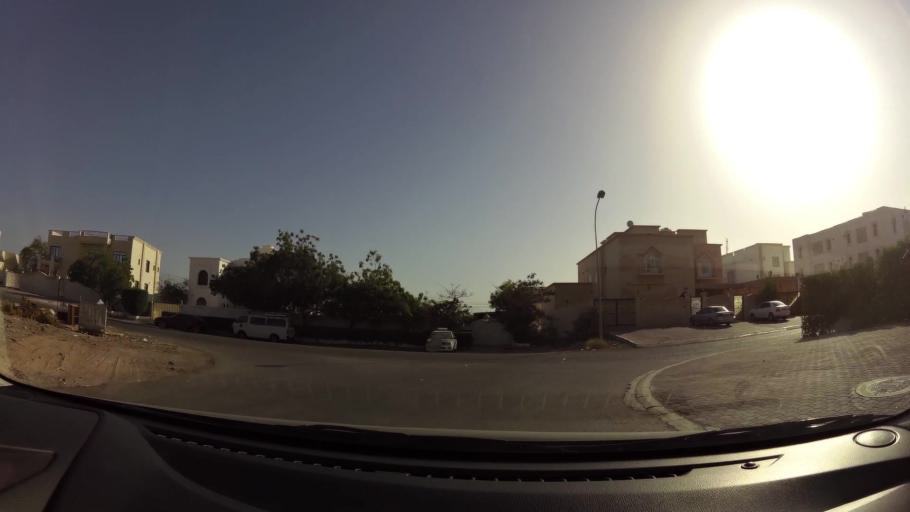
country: OM
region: Muhafazat Masqat
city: As Sib al Jadidah
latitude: 23.5955
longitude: 58.2043
